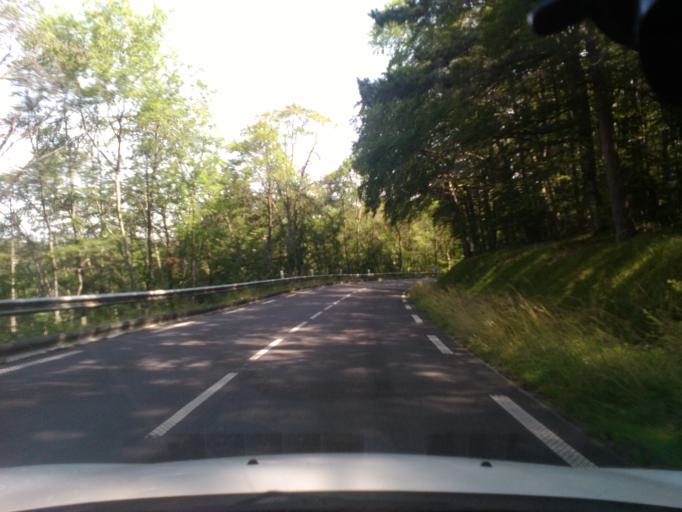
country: FR
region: Lorraine
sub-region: Departement des Vosges
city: Neufchateau
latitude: 48.3512
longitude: 5.7153
